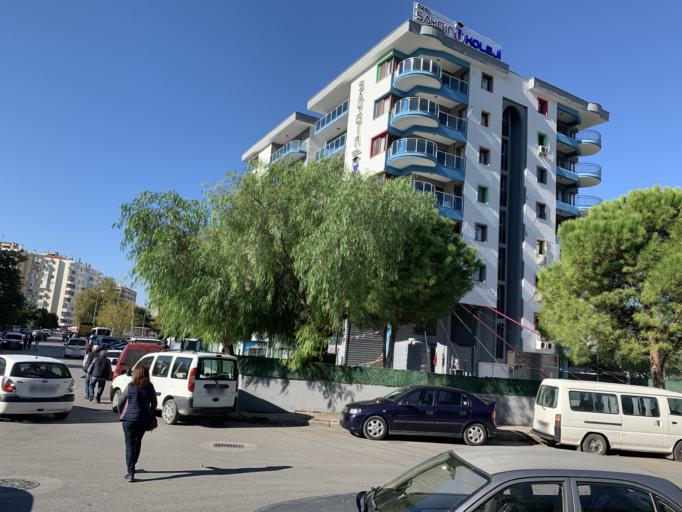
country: TR
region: Izmir
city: Bornova
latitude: 38.4598
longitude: 27.1860
